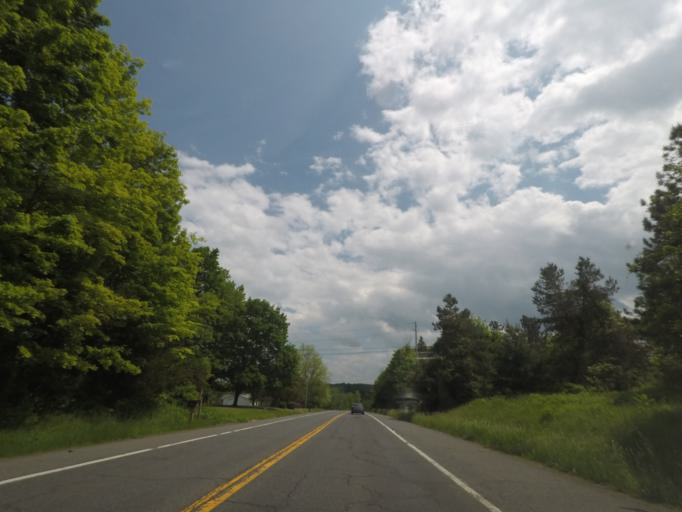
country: US
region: New York
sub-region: Columbia County
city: Oakdale
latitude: 42.1350
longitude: -73.7314
